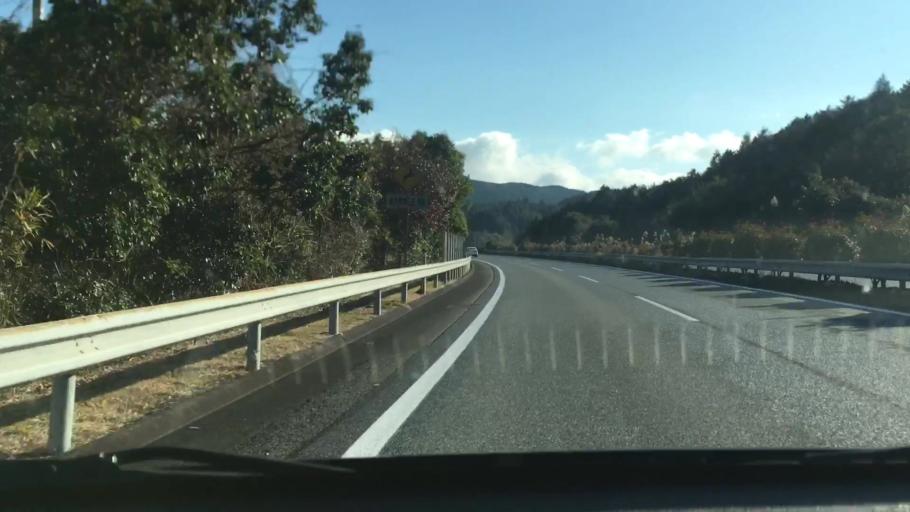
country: JP
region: Kumamoto
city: Hitoyoshi
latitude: 32.1879
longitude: 130.7769
